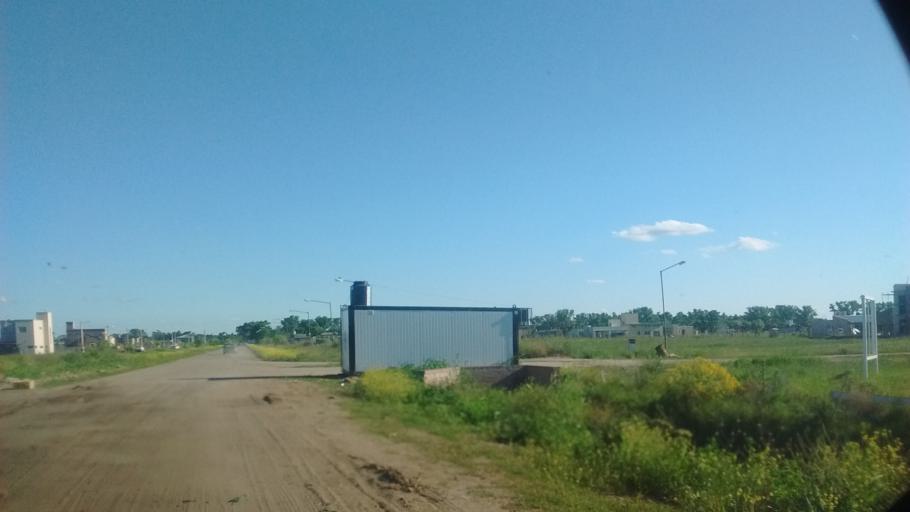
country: AR
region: Santa Fe
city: Funes
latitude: -32.8982
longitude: -60.8050
